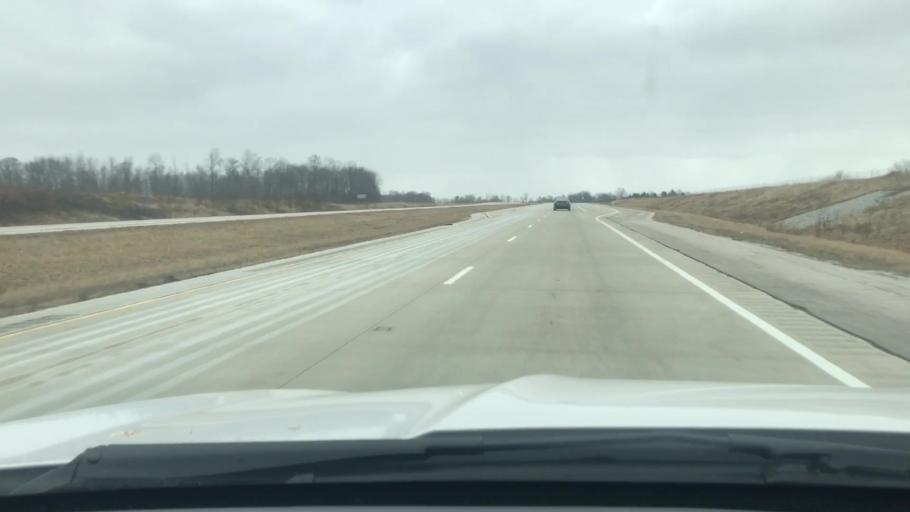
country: US
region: Indiana
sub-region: Carroll County
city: Delphi
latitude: 40.5152
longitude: -86.7218
